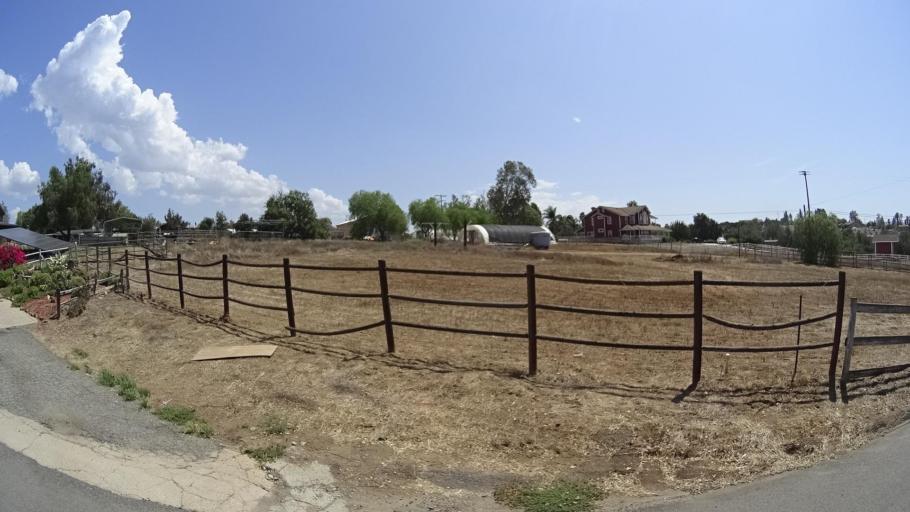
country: US
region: California
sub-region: San Diego County
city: Valley Center
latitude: 33.2465
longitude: -116.9896
